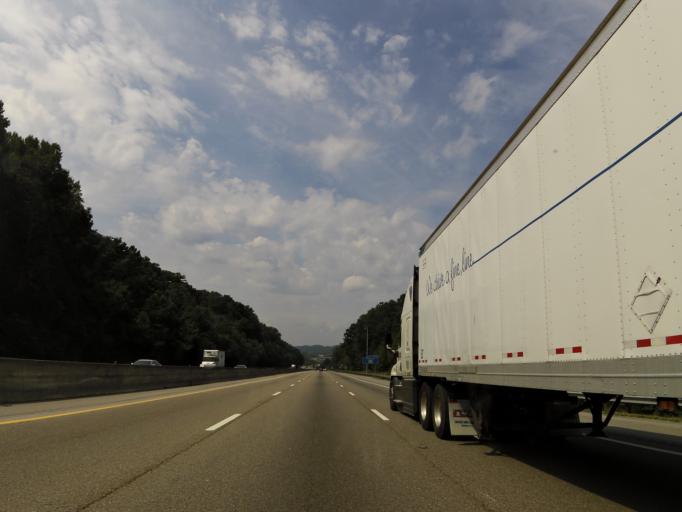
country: US
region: Tennessee
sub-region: Knox County
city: Farragut
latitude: 35.8884
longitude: -84.2141
